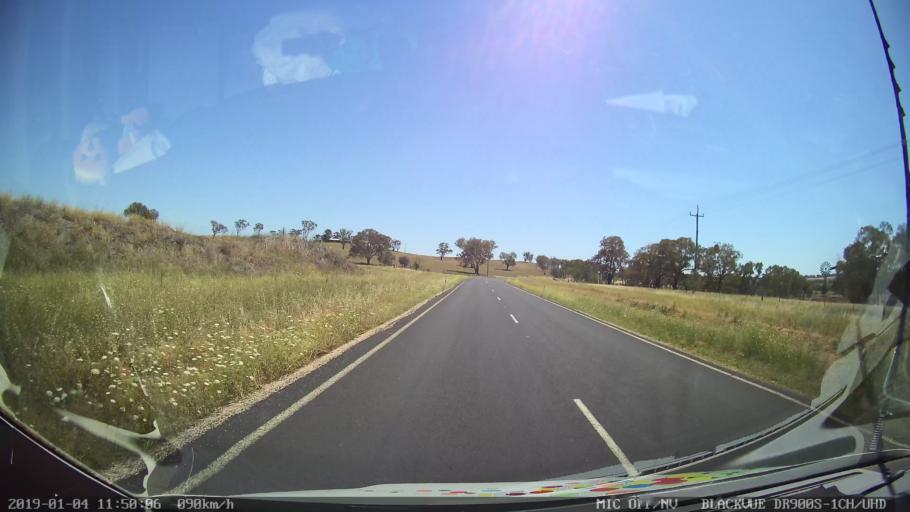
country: AU
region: New South Wales
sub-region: Cabonne
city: Molong
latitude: -32.9104
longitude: 148.7553
